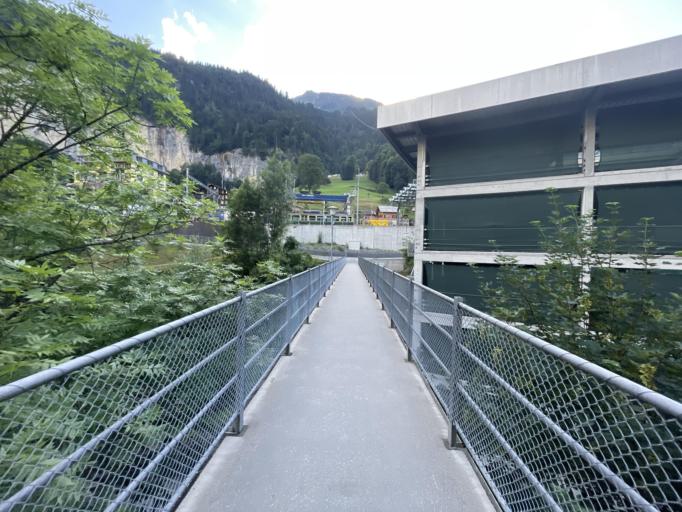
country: CH
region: Bern
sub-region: Interlaken-Oberhasli District
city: Lauterbrunnen
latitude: 46.5976
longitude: 7.9089
